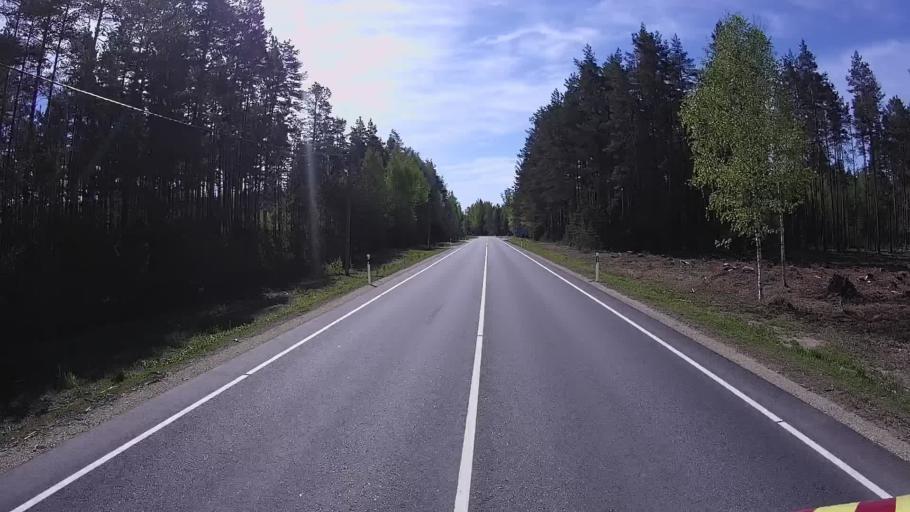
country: EE
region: Polvamaa
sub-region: Raepina vald
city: Rapina
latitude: 57.9798
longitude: 27.5695
